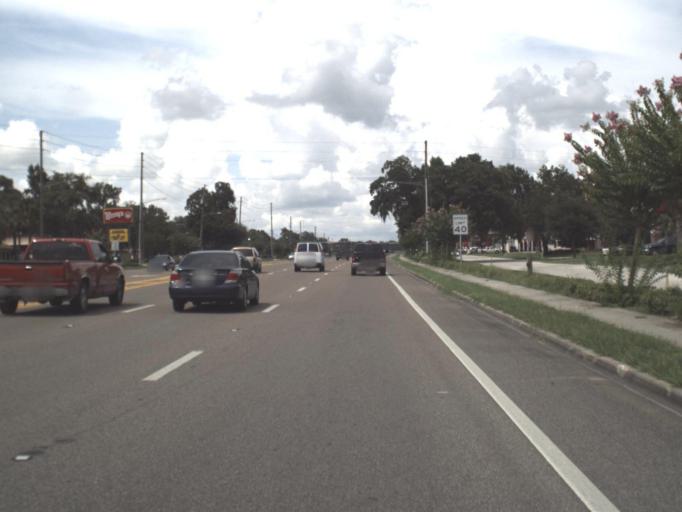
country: US
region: Florida
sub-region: Hernando County
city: South Brooksville
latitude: 28.5425
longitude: -82.4024
